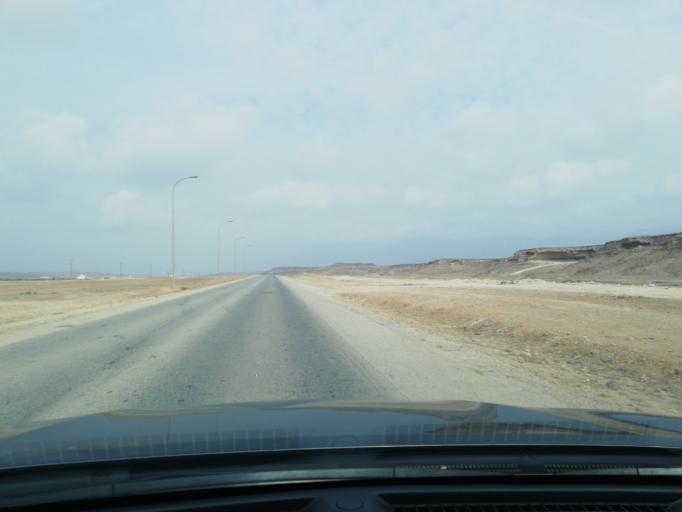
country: OM
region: Zufar
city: Salalah
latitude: 16.9543
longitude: 53.9176
